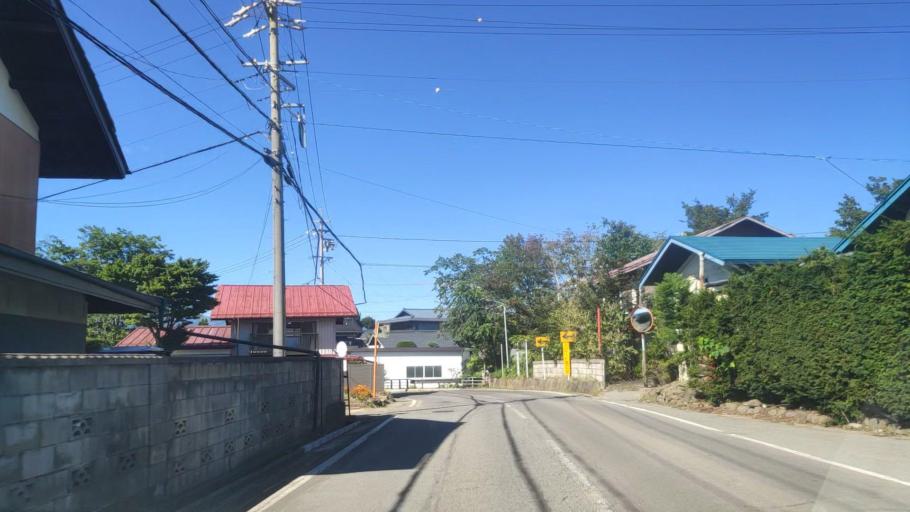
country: JP
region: Nagano
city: Chino
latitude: 35.9802
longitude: 138.2197
